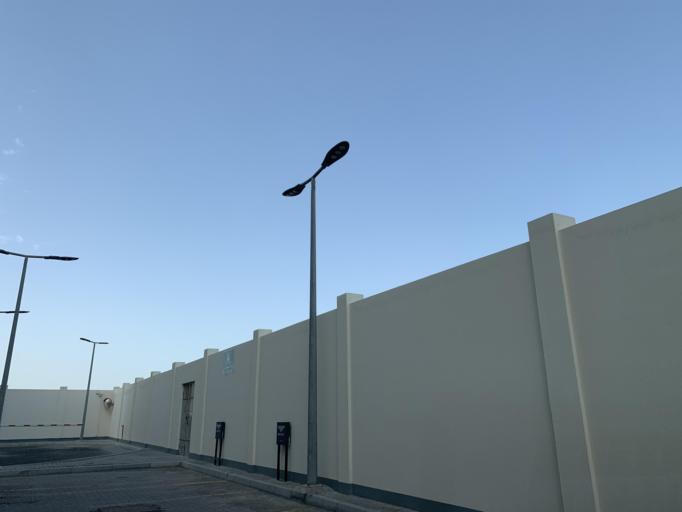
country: BH
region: Northern
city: Sitrah
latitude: 26.1535
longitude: 50.6078
